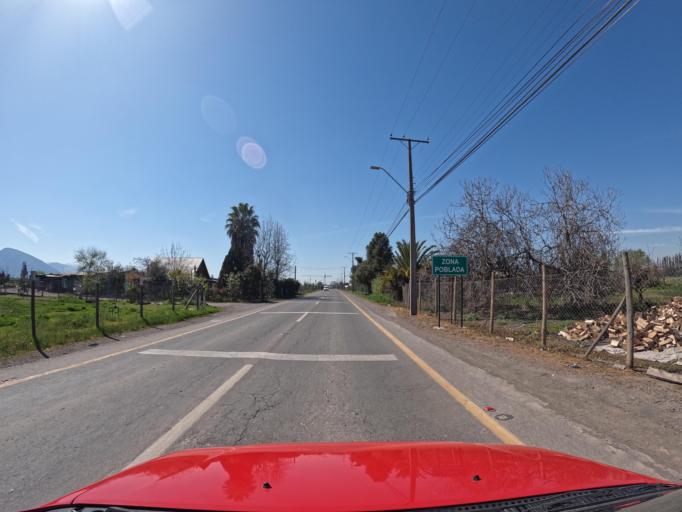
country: CL
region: Maule
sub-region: Provincia de Curico
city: Rauco
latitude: -35.0026
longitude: -71.3969
